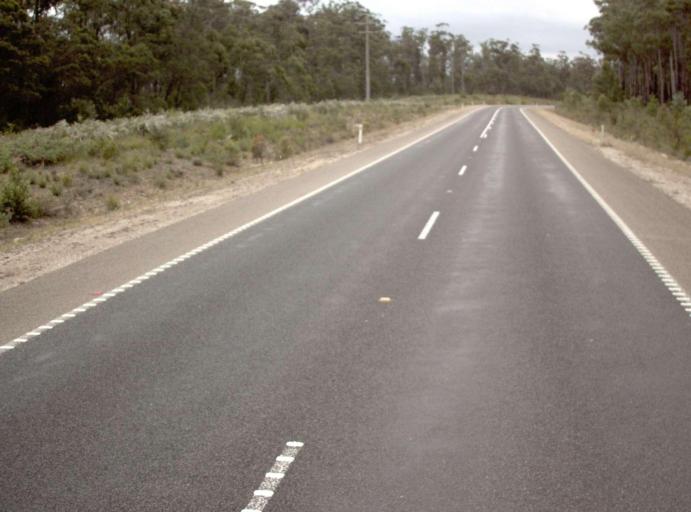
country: AU
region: Victoria
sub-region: East Gippsland
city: Lakes Entrance
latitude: -37.7055
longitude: 148.0610
